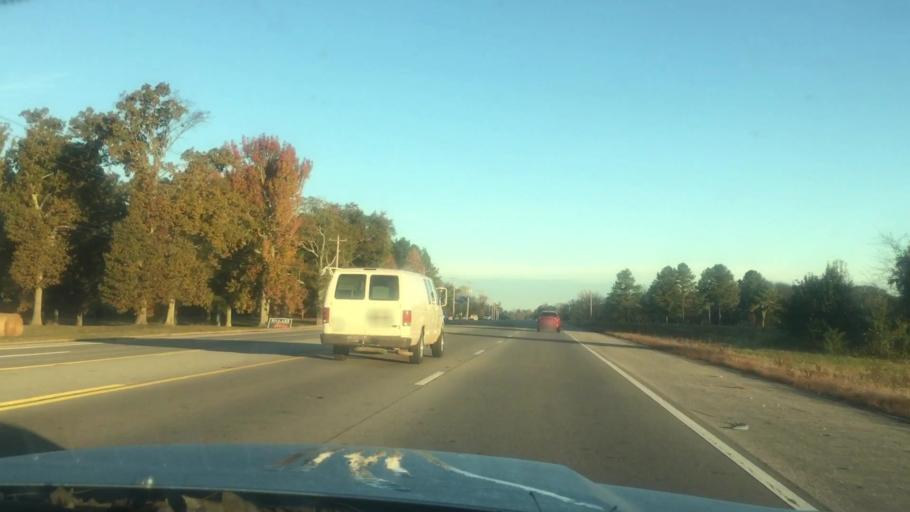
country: US
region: Tennessee
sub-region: Franklin County
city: Decherd
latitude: 35.2333
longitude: -86.1105
